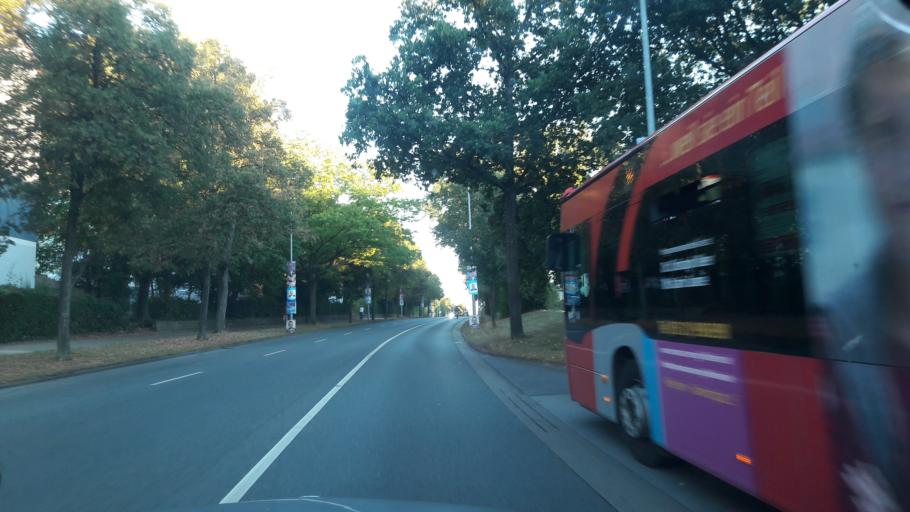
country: DE
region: Lower Saxony
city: Hildesheim
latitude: 52.1361
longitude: 9.9705
